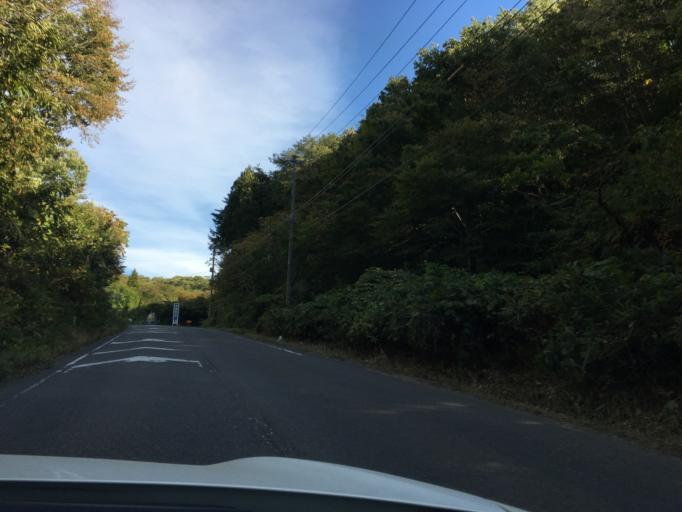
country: JP
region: Fukushima
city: Funehikimachi-funehiki
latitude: 37.3552
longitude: 140.5465
